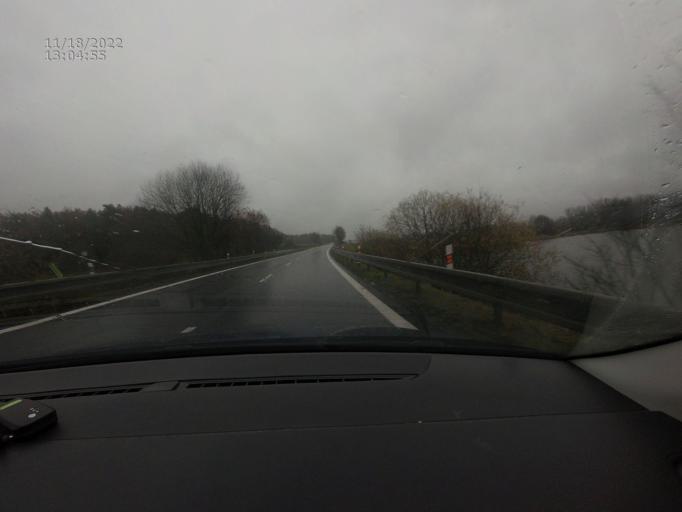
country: CZ
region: Plzensky
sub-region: Okres Klatovy
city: Planice
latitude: 49.3472
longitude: 13.4761
